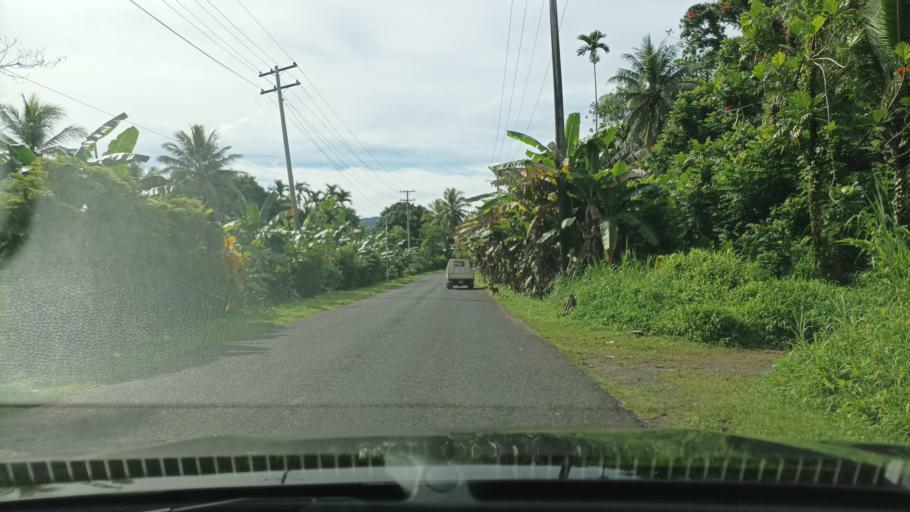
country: FM
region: Pohnpei
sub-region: Kolonia Municipality
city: Kolonia Town
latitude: 6.9489
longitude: 158.1944
